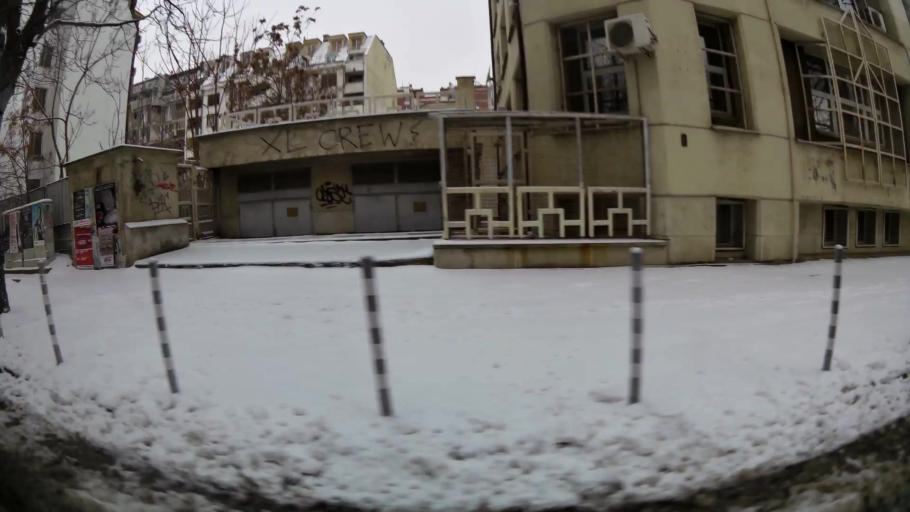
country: BG
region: Sofia-Capital
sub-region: Stolichna Obshtina
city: Sofia
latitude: 42.7038
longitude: 23.3053
